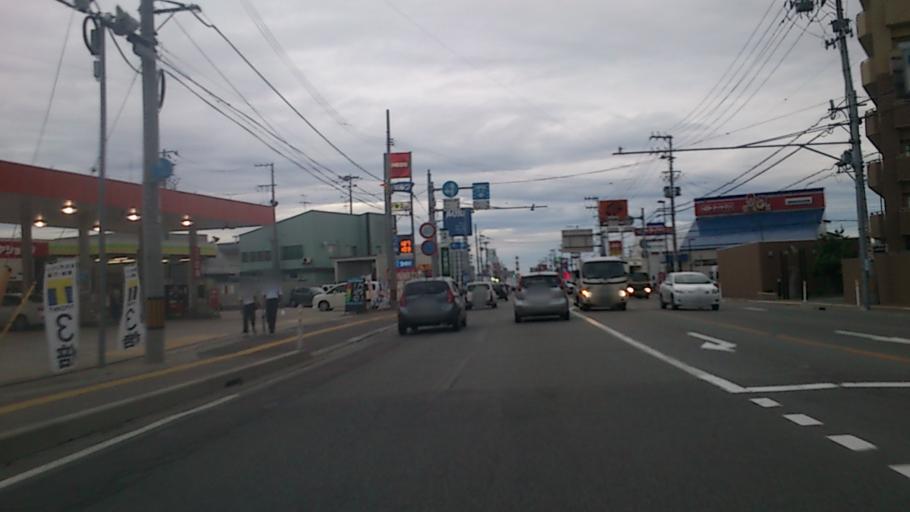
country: JP
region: Akita
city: Akita Shi
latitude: 39.7368
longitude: 140.0980
